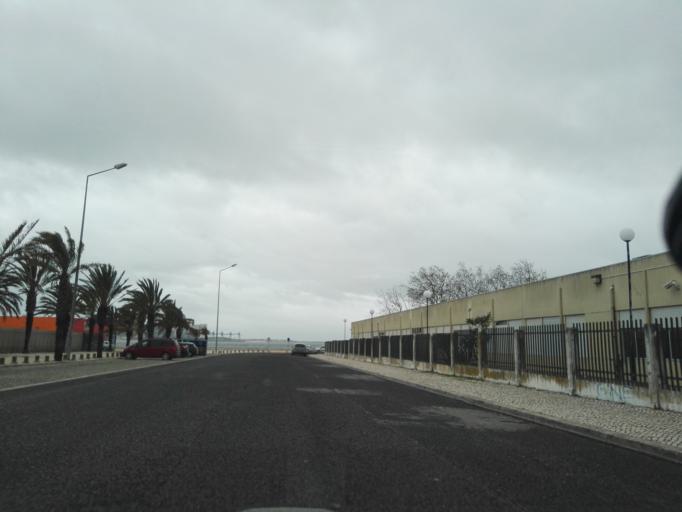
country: PT
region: Lisbon
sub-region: Oeiras
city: Alges
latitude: 38.6967
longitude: -9.2301
